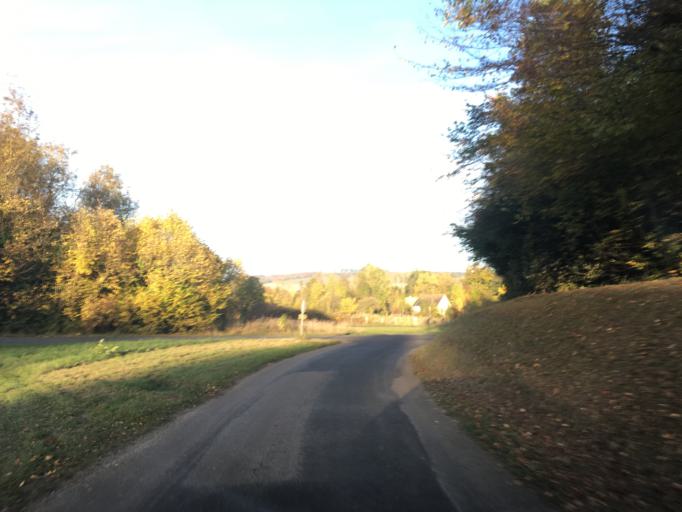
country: FR
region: Haute-Normandie
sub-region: Departement de l'Eure
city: Heudreville-sur-Eure
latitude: 49.1021
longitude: 1.2298
